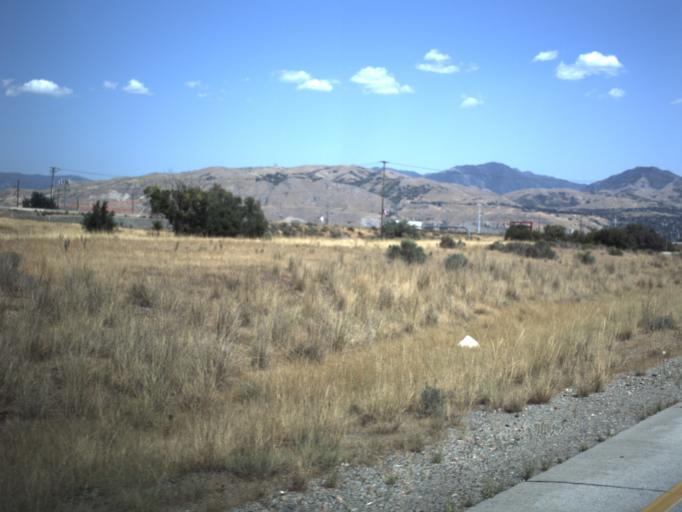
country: US
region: Utah
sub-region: Salt Lake County
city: Salt Lake City
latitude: 40.7648
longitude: -111.9465
